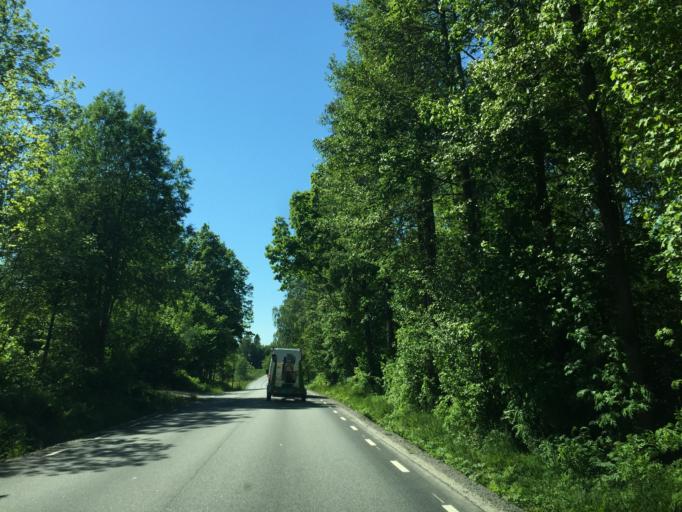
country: SE
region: OErebro
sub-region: Askersunds Kommun
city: Askersund
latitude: 58.8616
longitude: 15.0209
